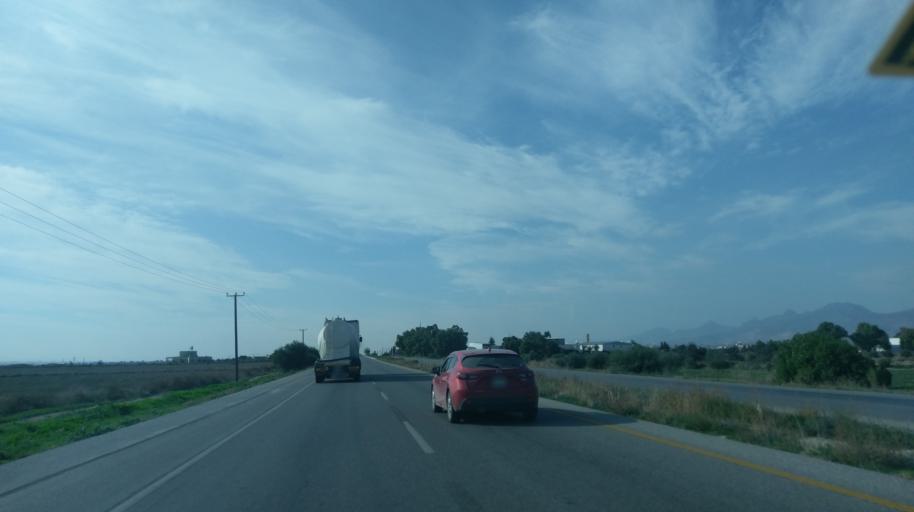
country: CY
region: Larnaka
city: Athienou
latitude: 35.2114
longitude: 33.5327
